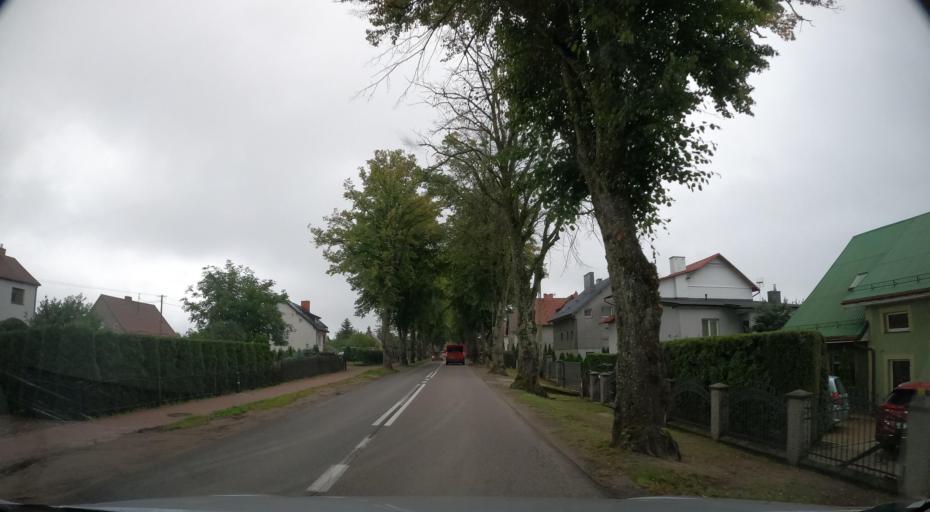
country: PL
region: Pomeranian Voivodeship
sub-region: Powiat wejherowski
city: Linia
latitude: 54.4570
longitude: 18.0172
